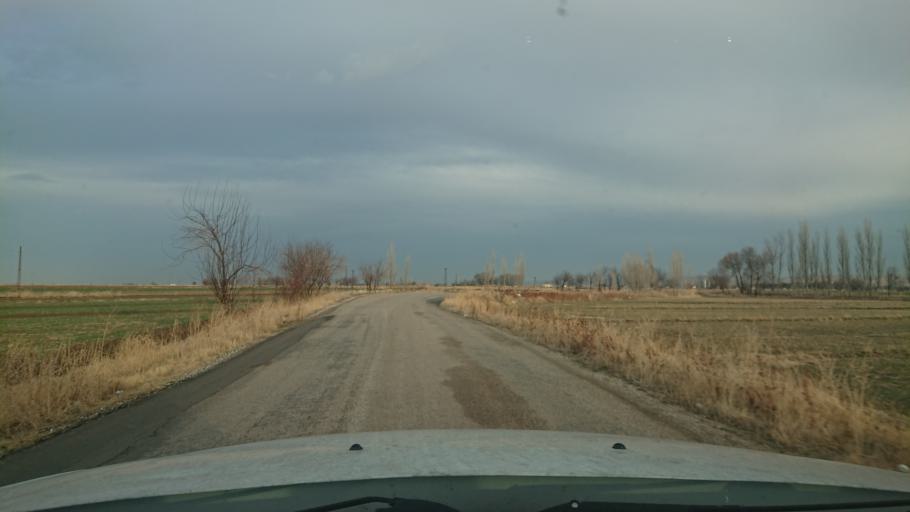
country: TR
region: Aksaray
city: Yesilova
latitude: 38.4412
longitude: 33.8369
